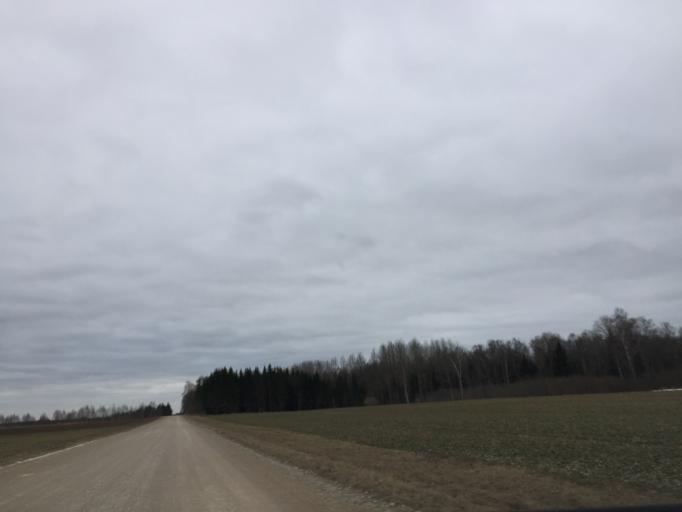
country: LT
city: Zagare
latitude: 56.3073
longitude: 23.2559
